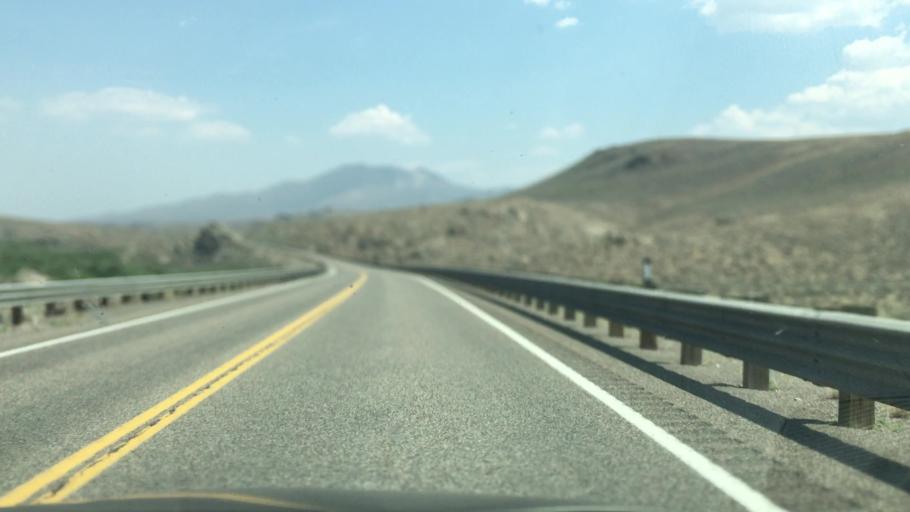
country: US
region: Nevada
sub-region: Elko County
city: Jackpot
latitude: 41.7424
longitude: -114.7751
